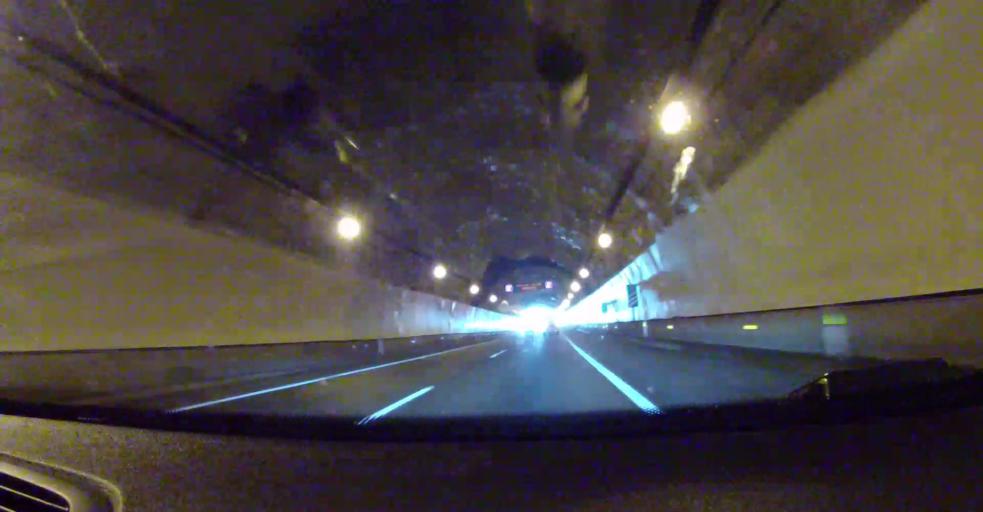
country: ES
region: Basque Country
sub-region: Provincia de Guipuzcoa
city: Arrasate / Mondragon
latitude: 43.0754
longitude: -2.4584
